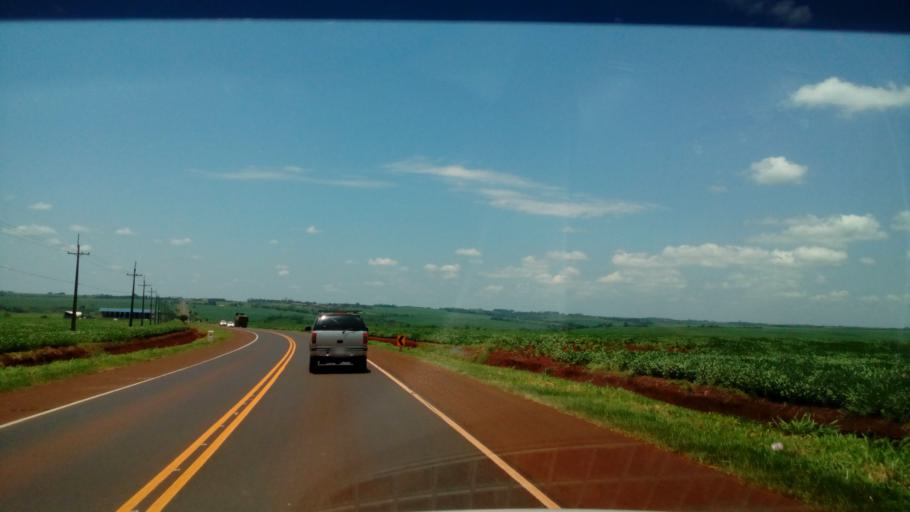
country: PY
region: Alto Parana
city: Naranjal
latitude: -25.8890
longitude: -55.1231
